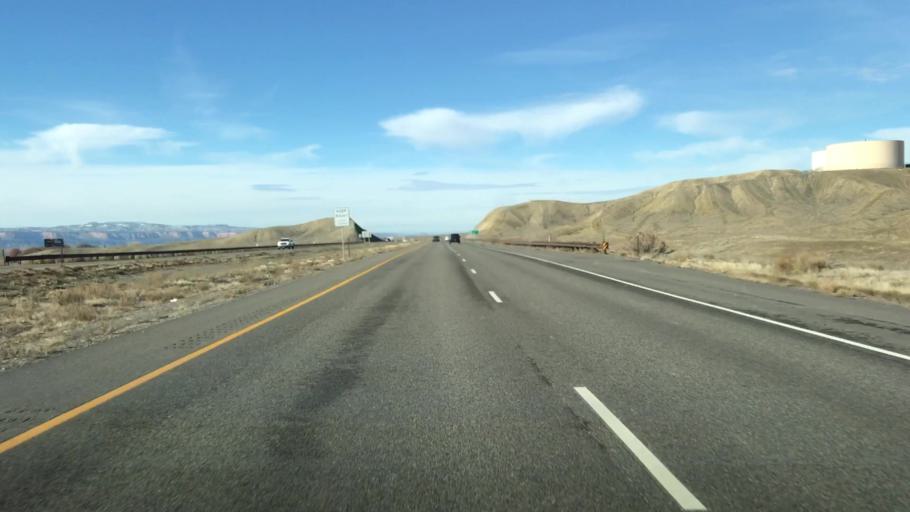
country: US
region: Colorado
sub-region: Mesa County
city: Clifton
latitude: 39.1020
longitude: -108.4570
